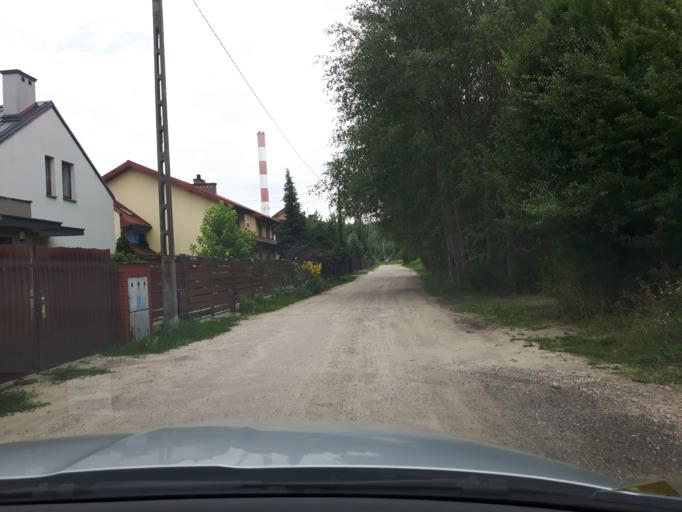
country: PL
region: Masovian Voivodeship
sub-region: Powiat wolominski
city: Zabki
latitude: 52.2782
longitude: 21.1220
